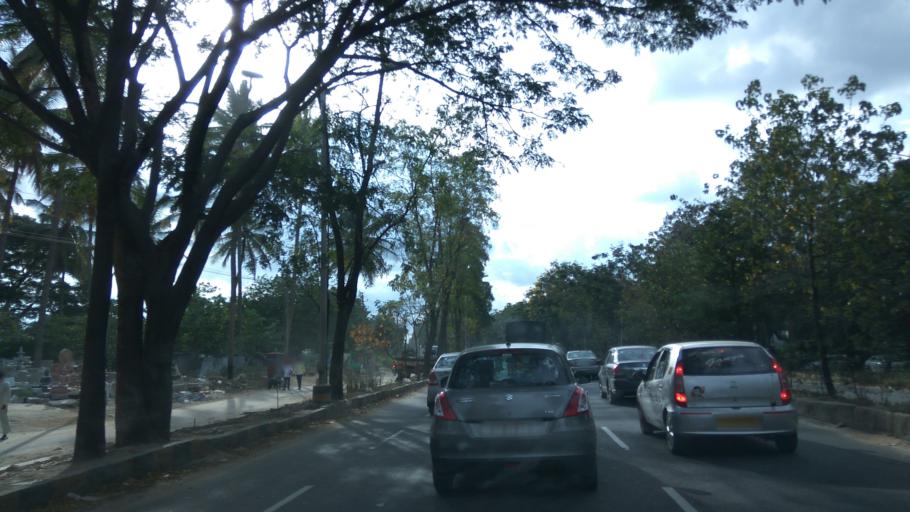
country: IN
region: Karnataka
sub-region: Bangalore Urban
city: Yelahanka
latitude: 13.0434
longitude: 77.6079
